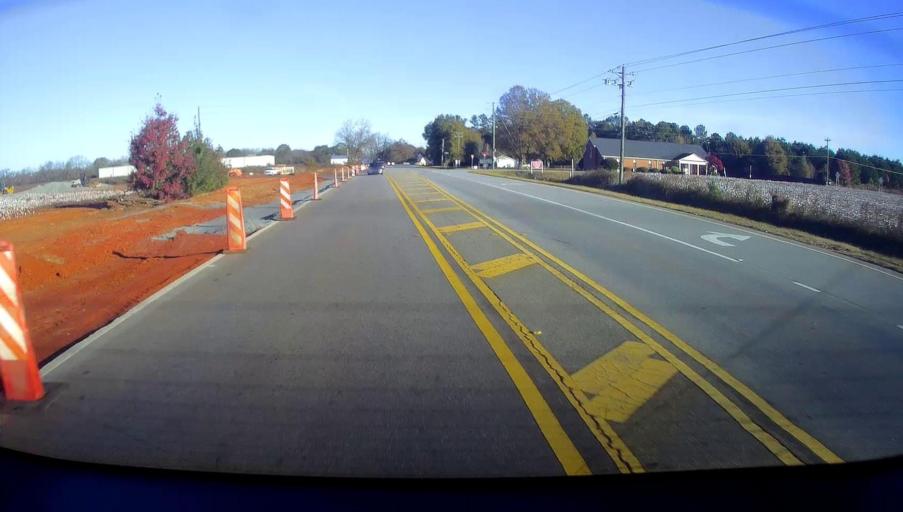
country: US
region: Georgia
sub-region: Houston County
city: Centerville
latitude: 32.5950
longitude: -83.7191
